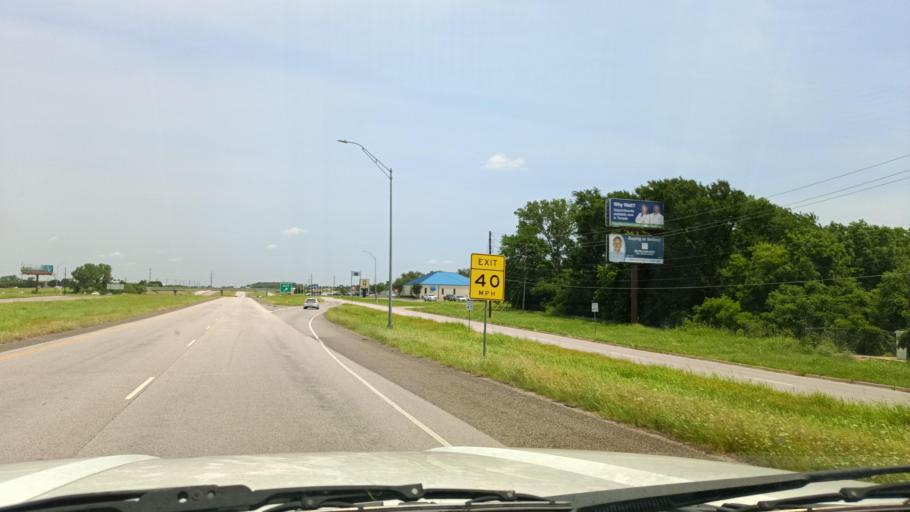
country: US
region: Texas
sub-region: Bell County
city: Temple
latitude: 31.1051
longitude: -97.3918
